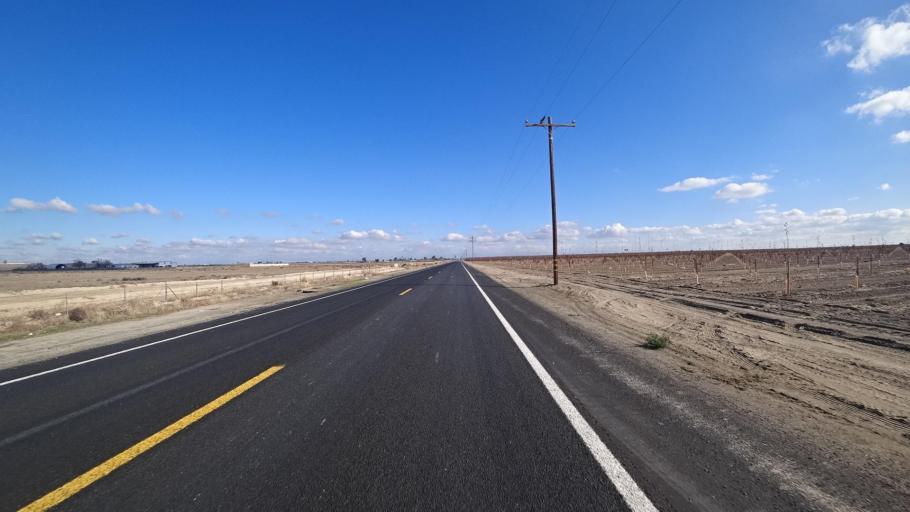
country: US
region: California
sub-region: Kern County
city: Delano
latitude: 35.7621
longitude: -119.3071
